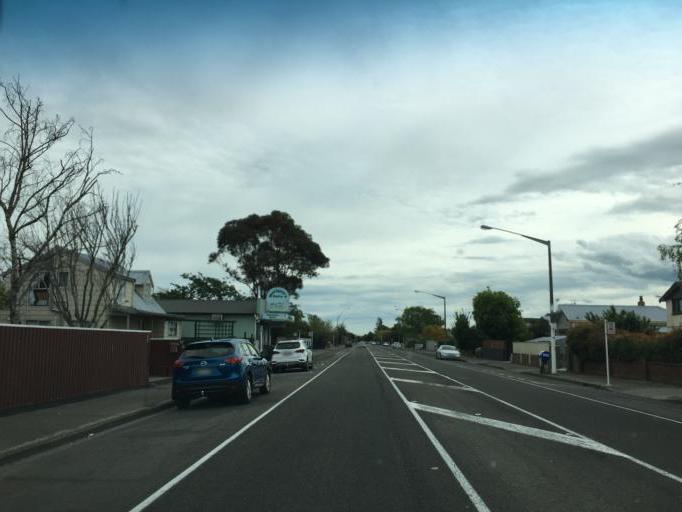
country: NZ
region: Manawatu-Wanganui
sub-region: Palmerston North City
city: Palmerston North
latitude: -40.3543
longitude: 175.5965
